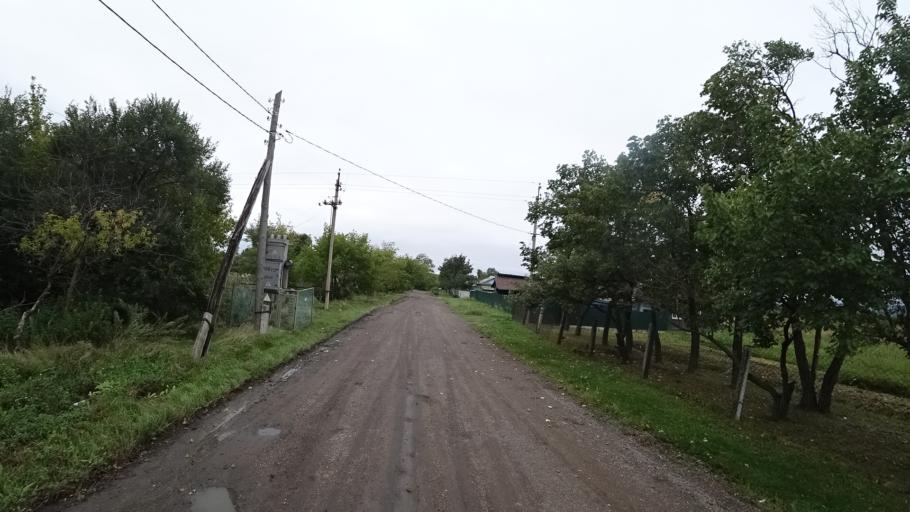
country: RU
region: Primorskiy
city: Chernigovka
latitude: 44.3297
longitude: 132.6000
